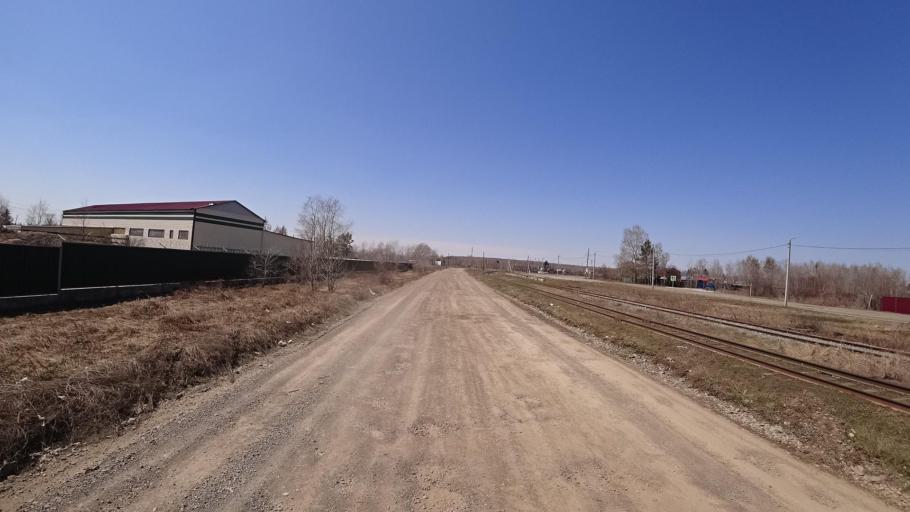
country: RU
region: Khabarovsk Krai
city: Khurba
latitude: 50.4086
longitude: 136.8894
